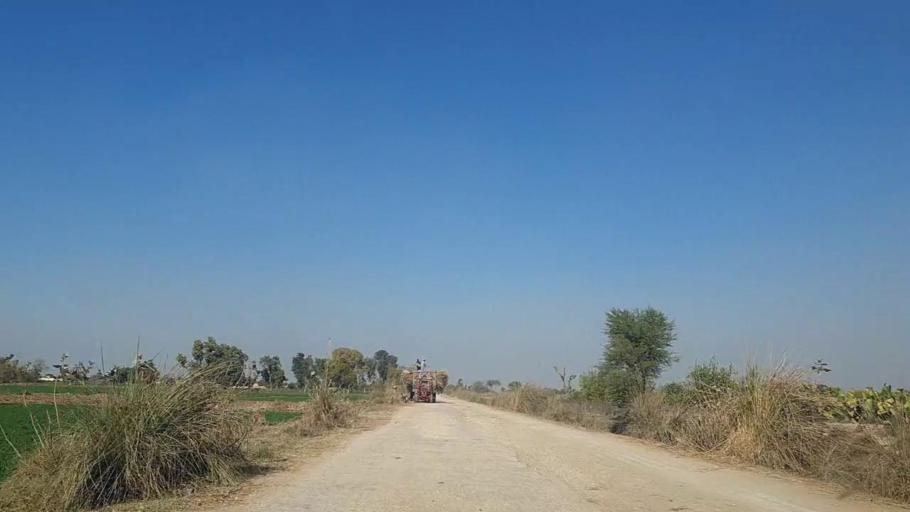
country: PK
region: Sindh
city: Sakrand
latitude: 26.2472
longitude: 68.2206
